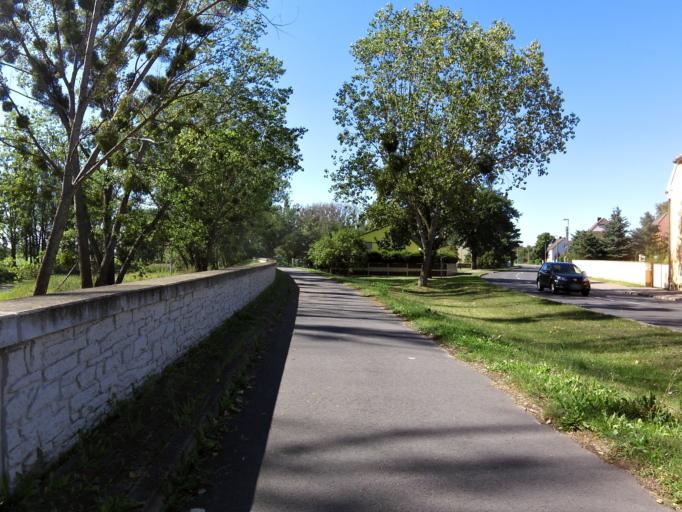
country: DE
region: Saxony-Anhalt
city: Elster
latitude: 51.8362
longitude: 12.7900
